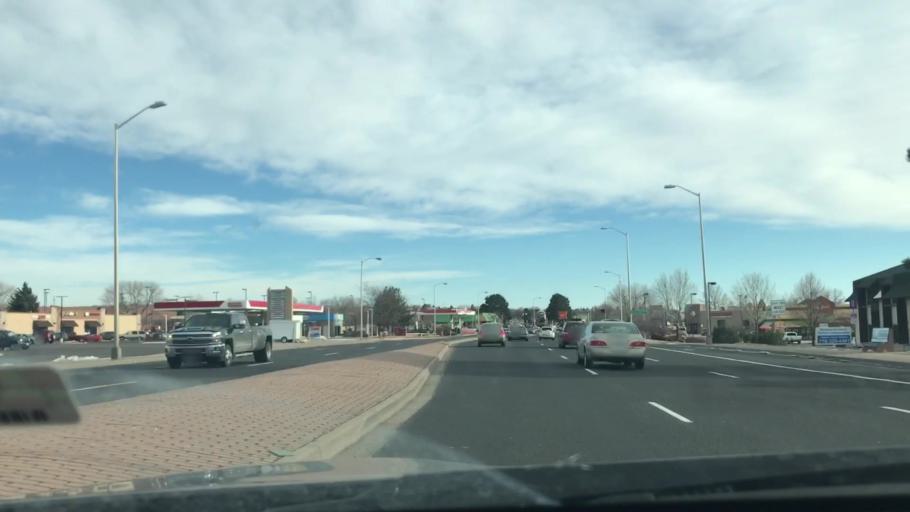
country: US
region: Colorado
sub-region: El Paso County
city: Cimarron Hills
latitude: 38.8954
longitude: -104.7594
